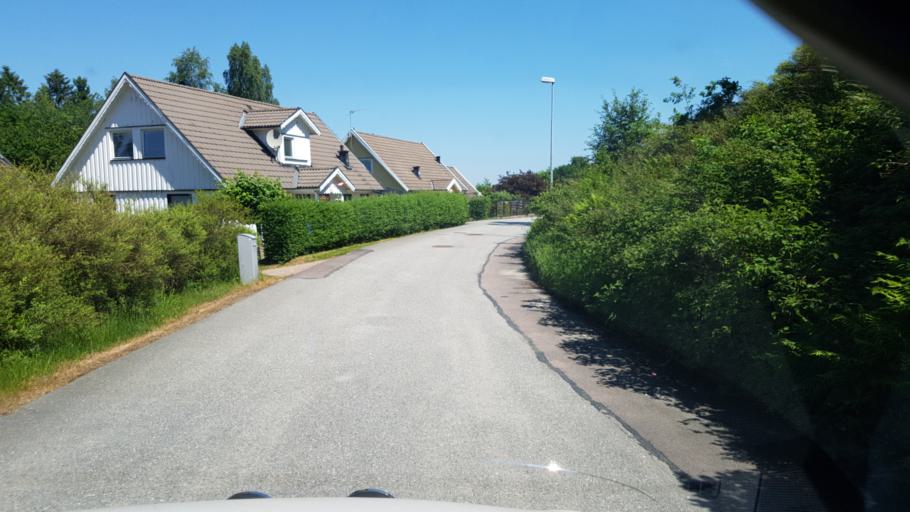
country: SE
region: Vaestra Goetaland
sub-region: Lerums Kommun
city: Stenkullen
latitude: 57.8032
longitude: 12.3544
